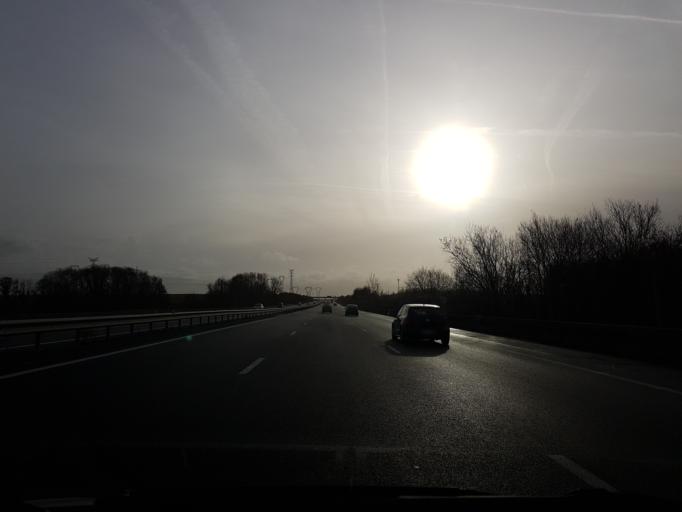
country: FR
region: Ile-de-France
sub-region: Departement de Seine-et-Marne
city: Moisenay
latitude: 48.5633
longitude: 2.7616
